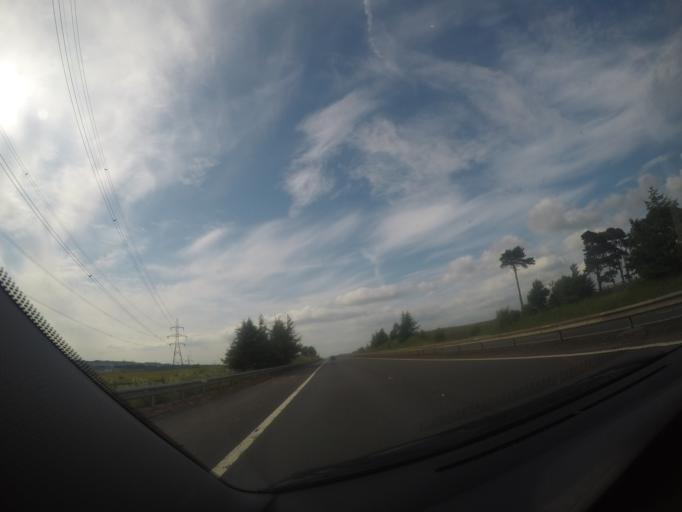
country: GB
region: Scotland
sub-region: South Lanarkshire
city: Lesmahagow
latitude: 55.6105
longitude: -3.8455
